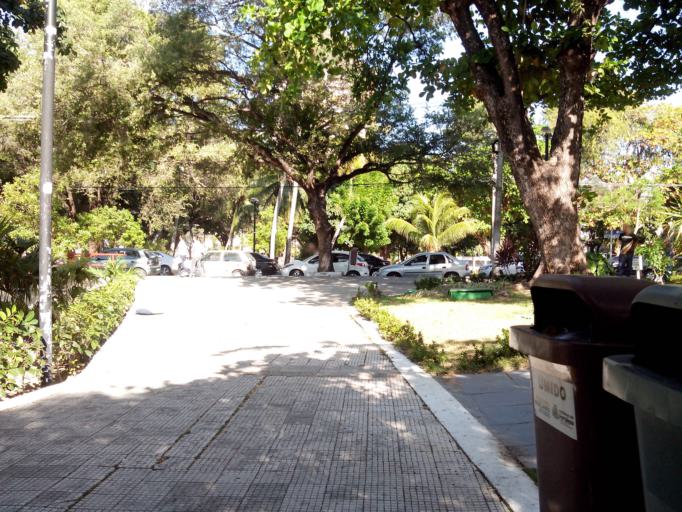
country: BR
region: Ceara
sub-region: Fortaleza
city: Fortaleza
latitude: -3.7316
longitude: -38.5233
